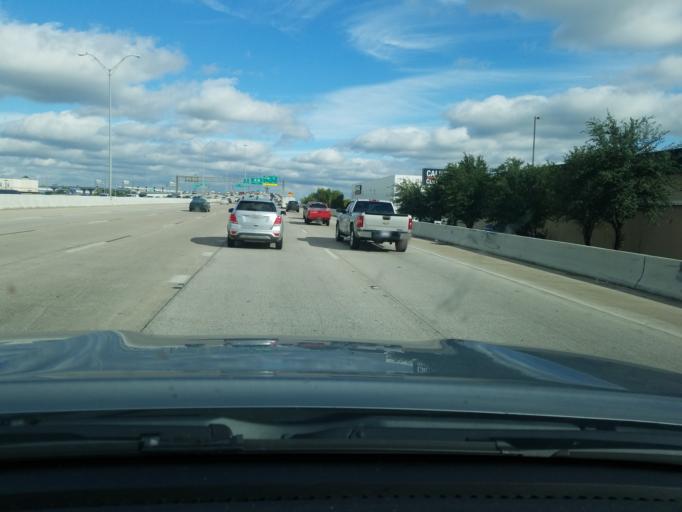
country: US
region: Texas
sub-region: Tarrant County
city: Fort Worth
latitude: 32.7446
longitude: -97.3298
